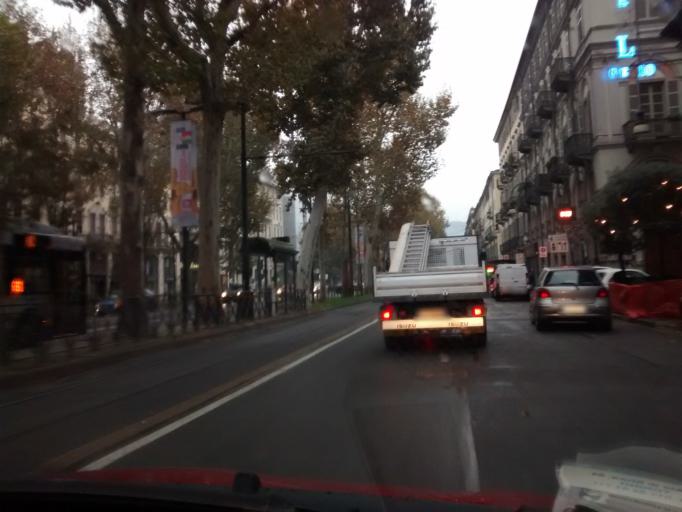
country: IT
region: Piedmont
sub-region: Provincia di Torino
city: Turin
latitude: 45.0621
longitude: 7.6804
